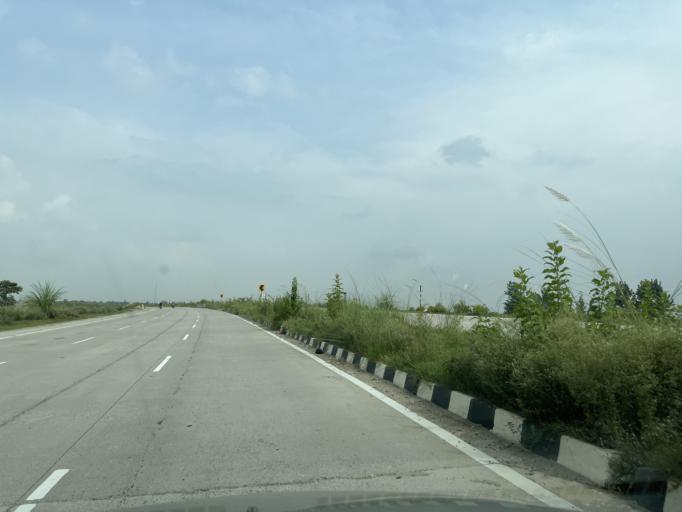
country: IN
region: Uttarakhand
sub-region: Udham Singh Nagar
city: Bazpur
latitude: 29.1469
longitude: 79.0297
